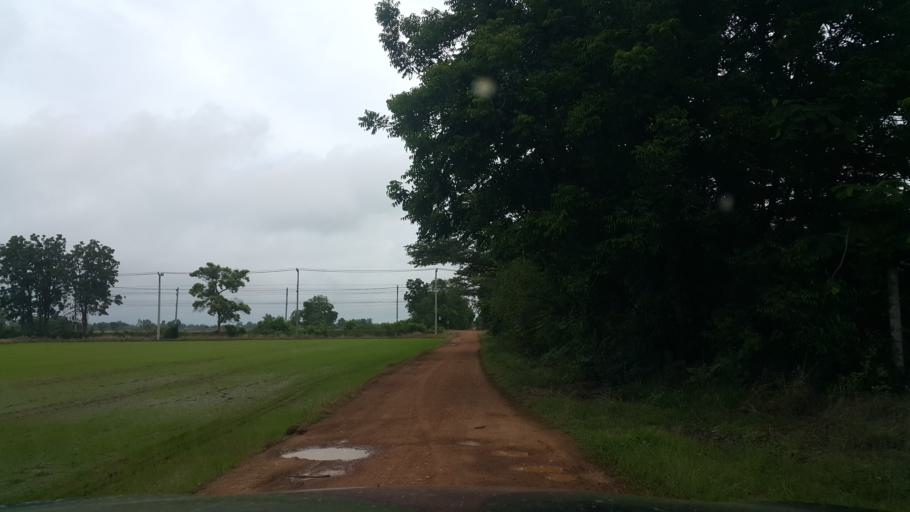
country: TH
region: Sukhothai
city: Sawankhalok
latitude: 17.3088
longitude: 99.7142
